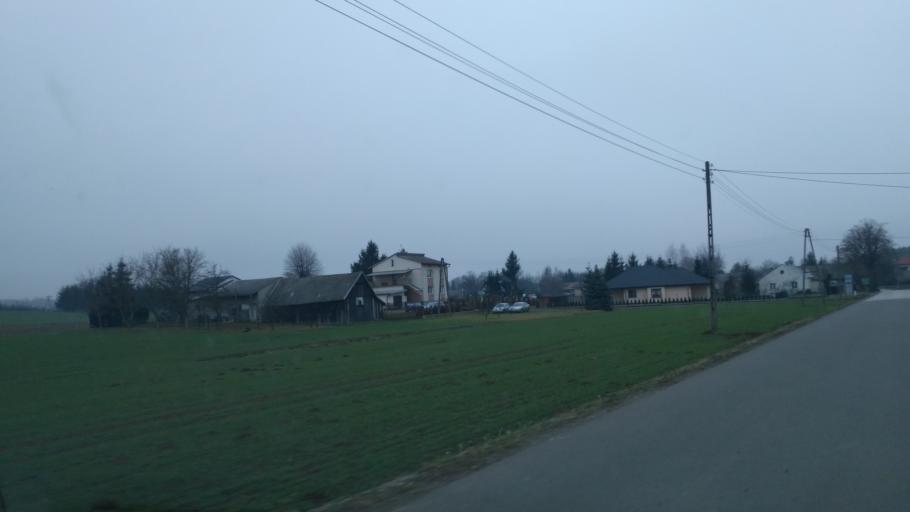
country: PL
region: Subcarpathian Voivodeship
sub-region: Powiat jaroslawski
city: Pawlosiow
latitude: 49.9716
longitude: 22.6392
